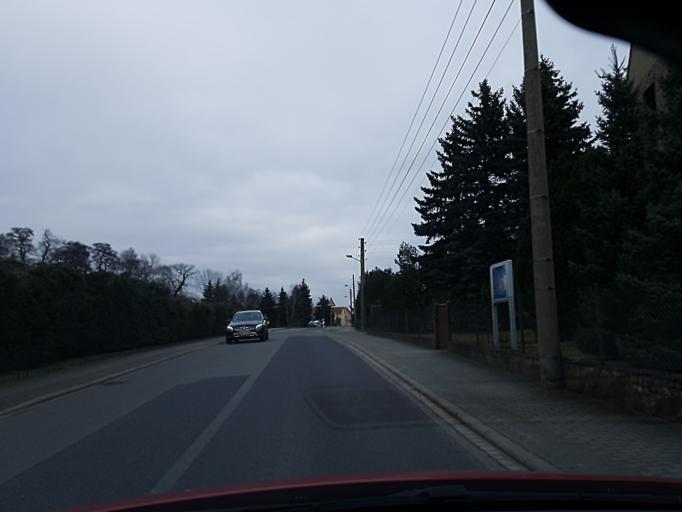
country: DE
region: Brandenburg
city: Merzdorf
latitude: 51.4023
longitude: 13.5352
